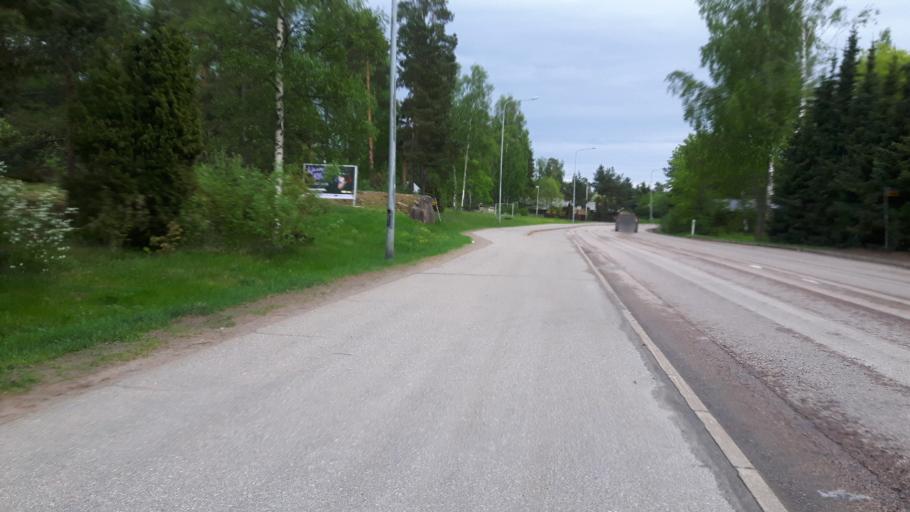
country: FI
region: Kymenlaakso
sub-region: Kotka-Hamina
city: Hamina
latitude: 60.5613
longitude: 27.2249
